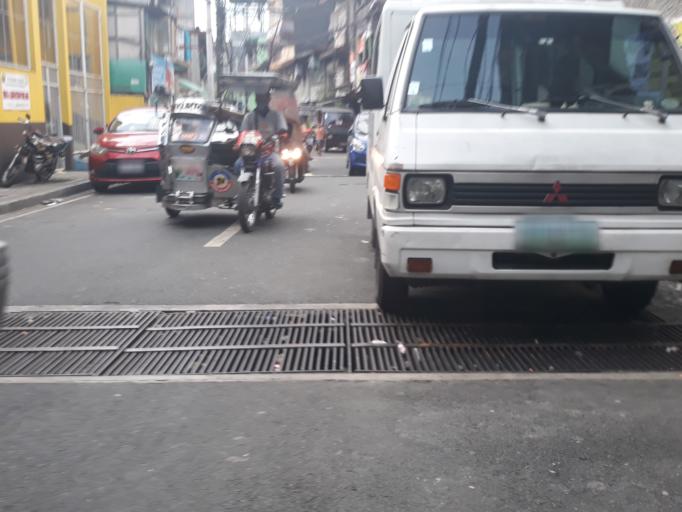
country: PH
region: Metro Manila
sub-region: San Juan
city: San Juan
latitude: 14.6080
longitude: 121.0228
